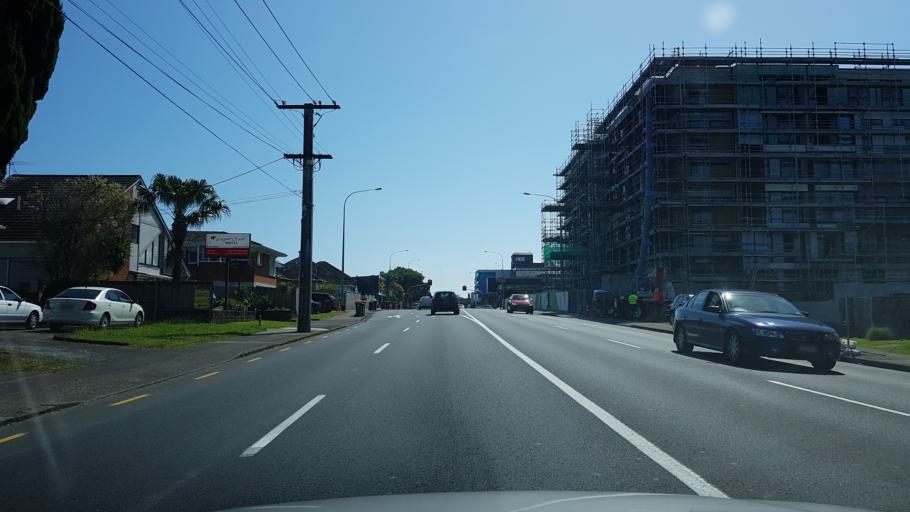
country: NZ
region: Auckland
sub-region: Auckland
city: North Shore
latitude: -36.7891
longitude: 174.7665
